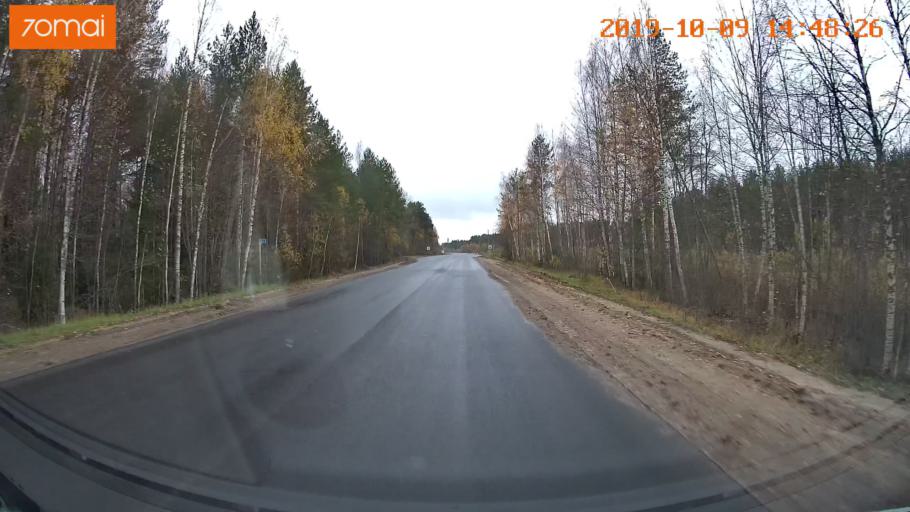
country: RU
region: Kostroma
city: Chistyye Bory
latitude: 58.4056
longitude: 41.5754
